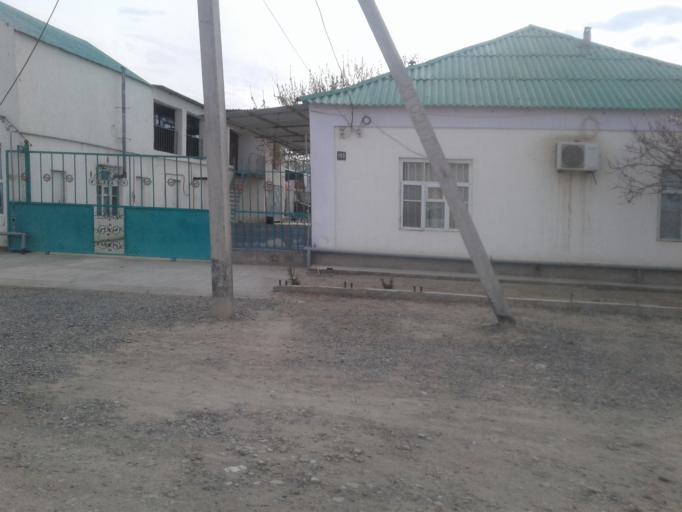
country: TM
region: Ahal
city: Abadan
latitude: 38.1204
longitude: 58.3515
